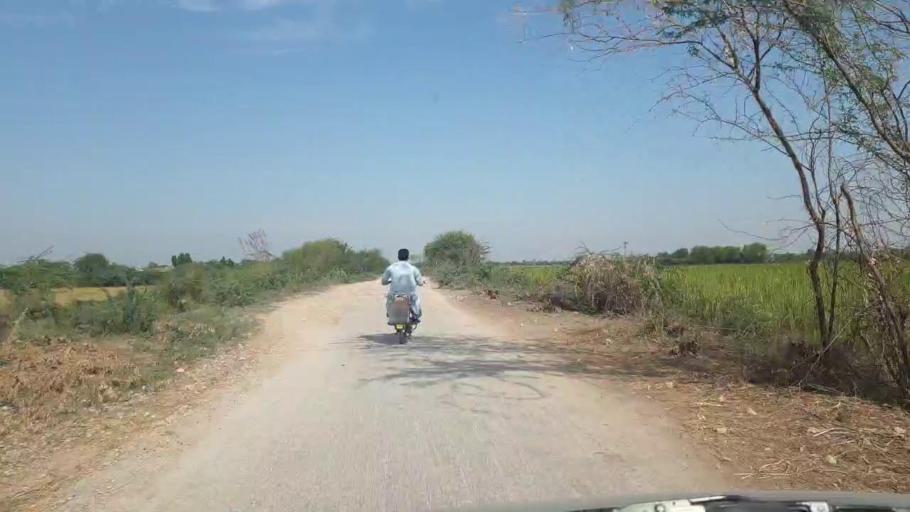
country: PK
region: Sindh
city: Tando Bago
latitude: 24.8656
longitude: 68.9975
